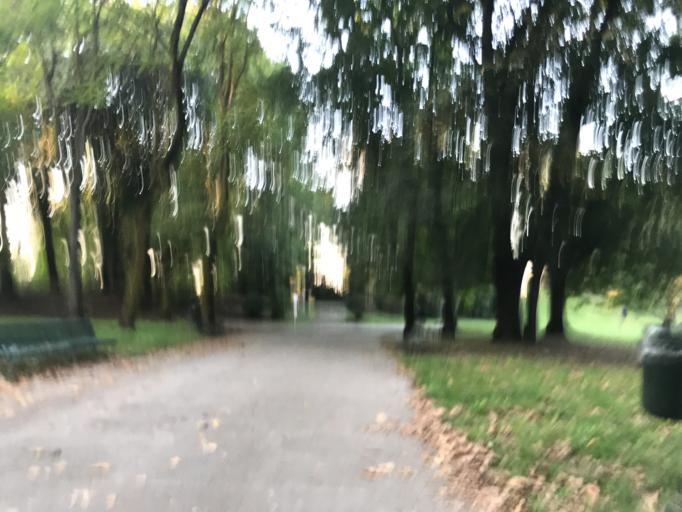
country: IT
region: Lombardy
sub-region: Citta metropolitana di Milano
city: Sesto San Giovanni
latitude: 45.4951
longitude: 9.2428
